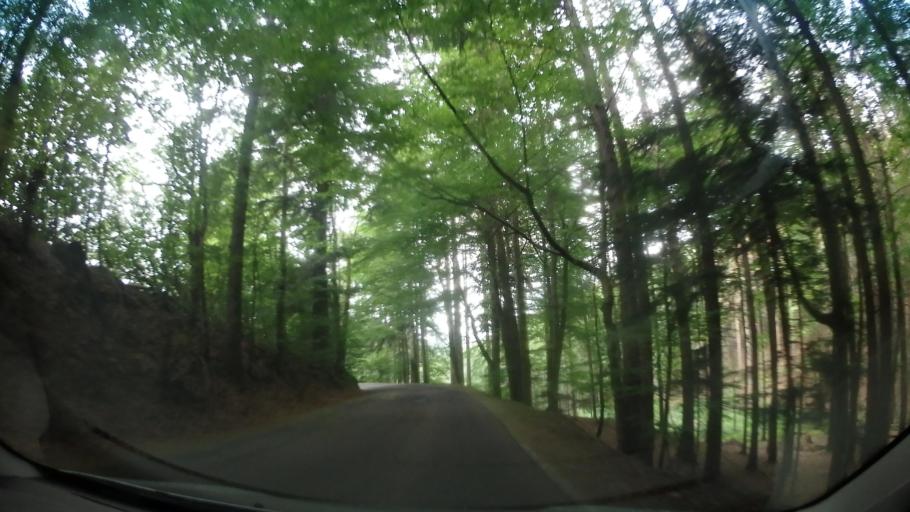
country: CZ
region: Pardubicky
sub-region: Okres Chrudim
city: Sec
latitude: 49.8298
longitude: 15.6975
